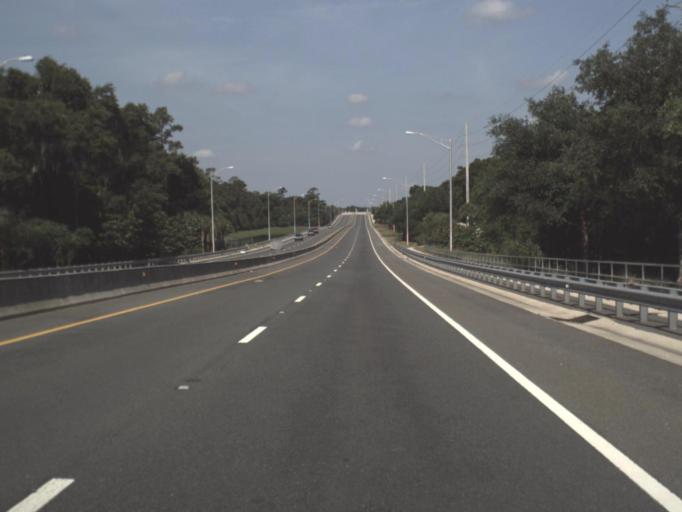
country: US
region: Florida
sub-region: Duval County
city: Atlantic Beach
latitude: 30.3597
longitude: -81.4485
